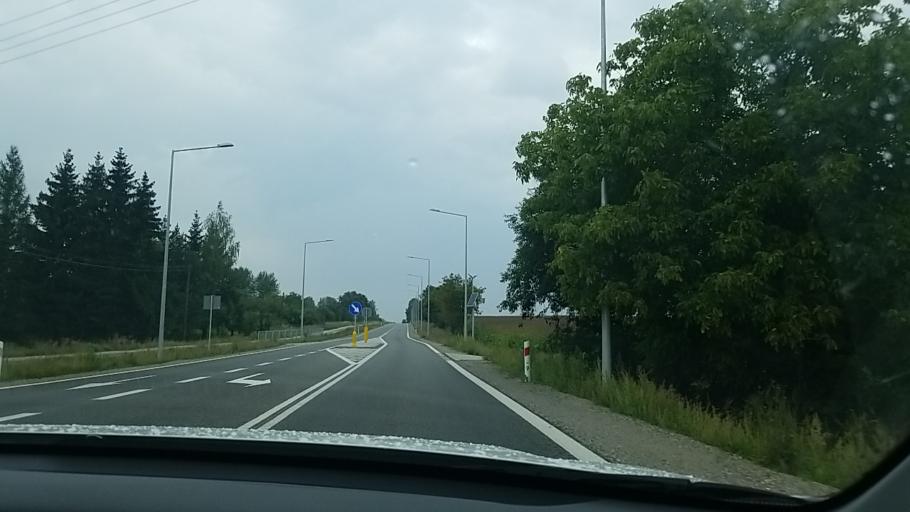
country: PL
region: Lublin Voivodeship
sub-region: Powiat lubelski
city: Krzczonow
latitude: 51.0042
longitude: 22.6727
